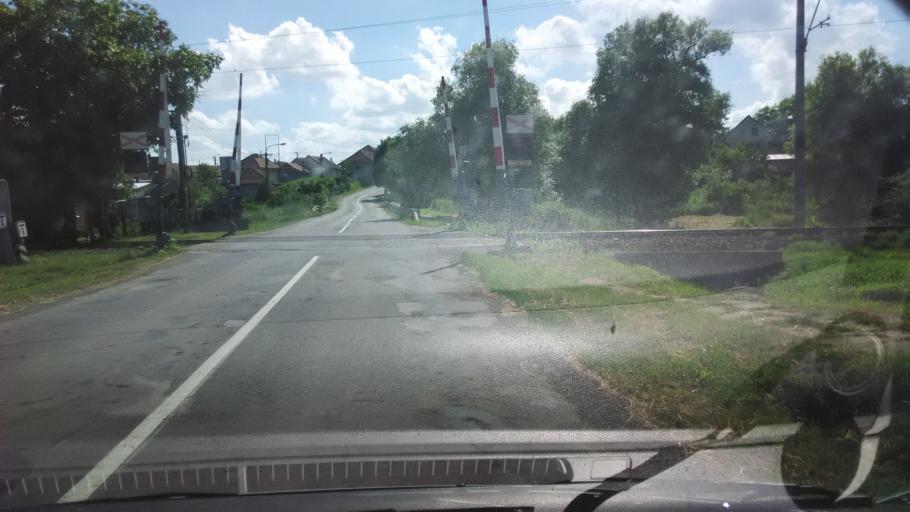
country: SK
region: Nitriansky
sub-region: Okres Nitra
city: Vrable
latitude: 48.1456
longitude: 18.4066
